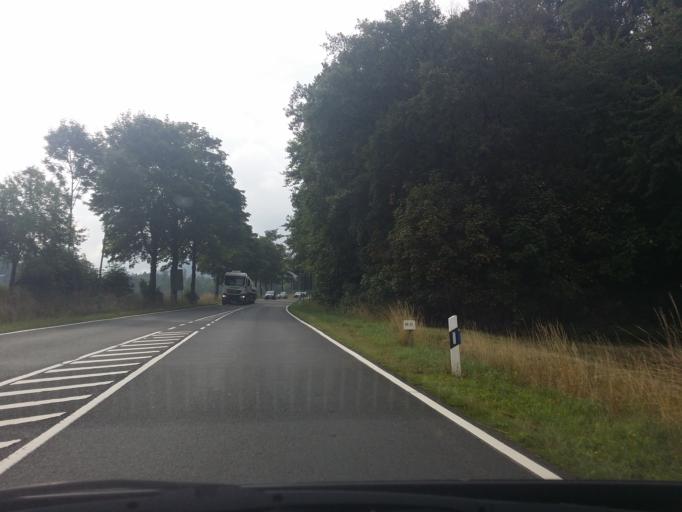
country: DE
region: Hesse
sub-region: Regierungsbezirk Darmstadt
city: Glashutten
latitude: 50.2329
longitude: 8.3976
